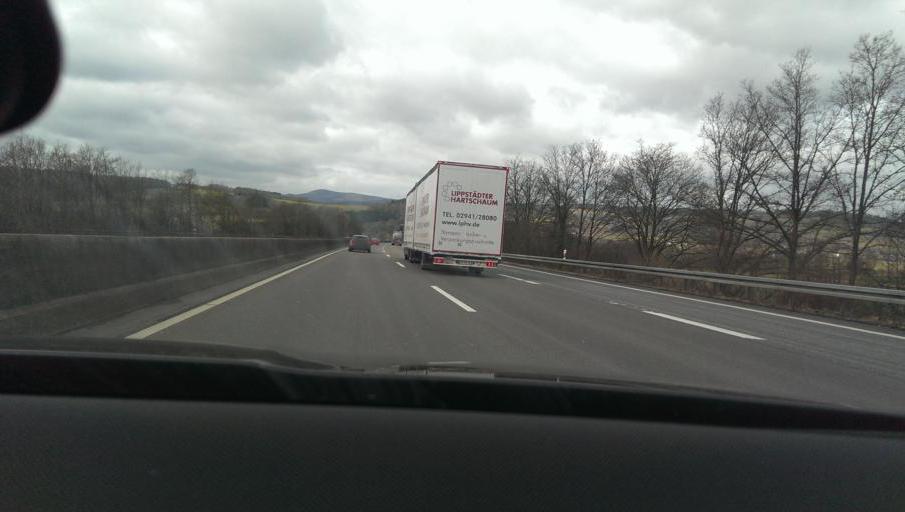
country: DE
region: Hesse
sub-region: Regierungsbezirk Kassel
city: Niederaula
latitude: 50.7614
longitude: 9.5992
